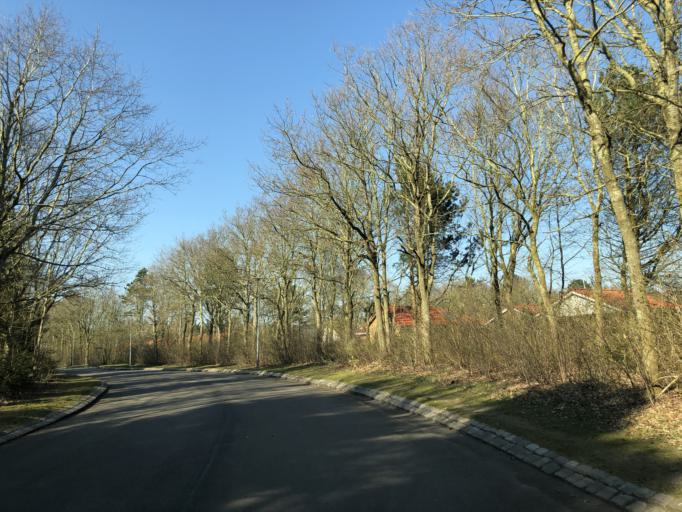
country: DK
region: Central Jutland
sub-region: Holstebro Kommune
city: Ulfborg
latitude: 56.3463
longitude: 8.3338
